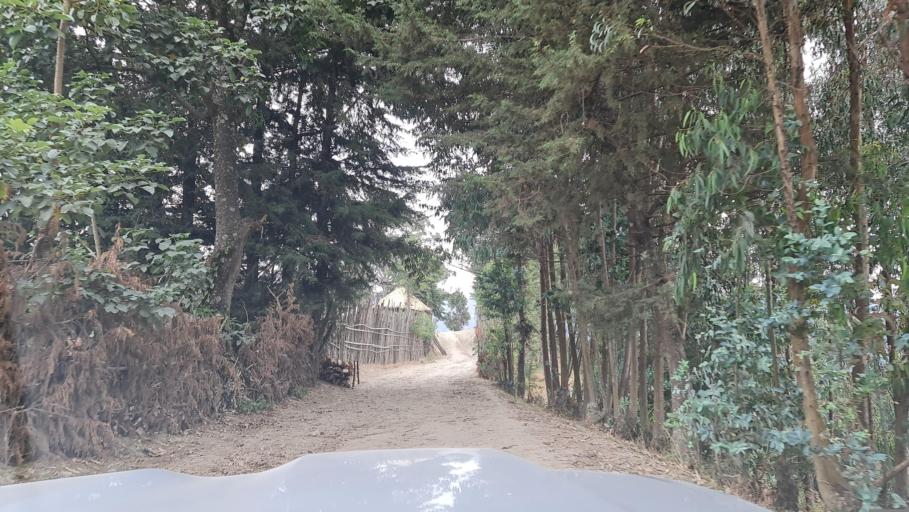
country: ET
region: Oromiya
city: Hagere Hiywet
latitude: 8.7988
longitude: 37.8891
